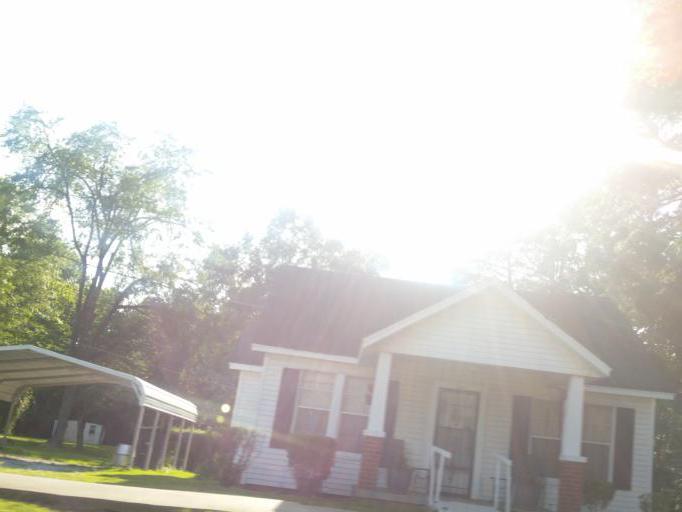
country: US
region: Mississippi
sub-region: Calhoun County
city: Calhoun City
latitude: 33.8525
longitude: -89.3114
